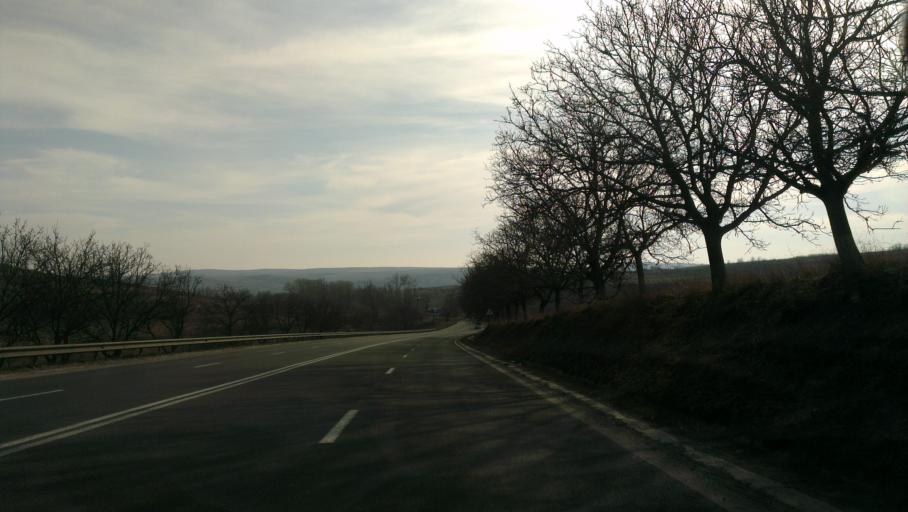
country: MD
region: Laloveni
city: Ialoveni
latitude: 46.9316
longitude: 28.7004
